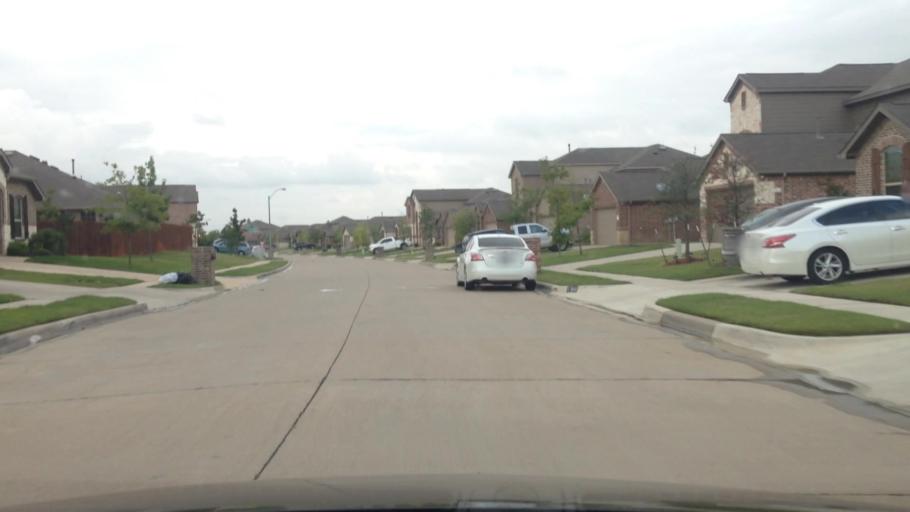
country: US
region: Texas
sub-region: Tarrant County
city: Crowley
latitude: 32.5675
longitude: -97.3390
